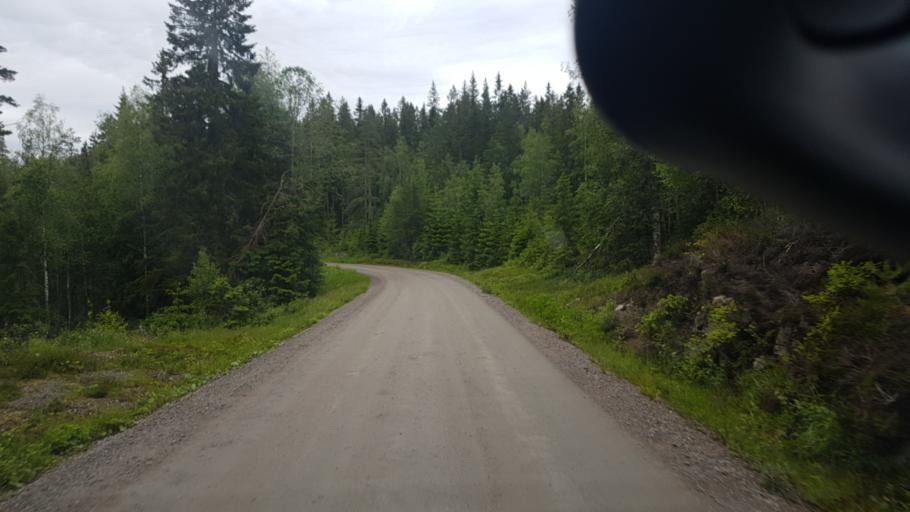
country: NO
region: Ostfold
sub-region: Romskog
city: Romskog
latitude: 59.7099
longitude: 12.0376
